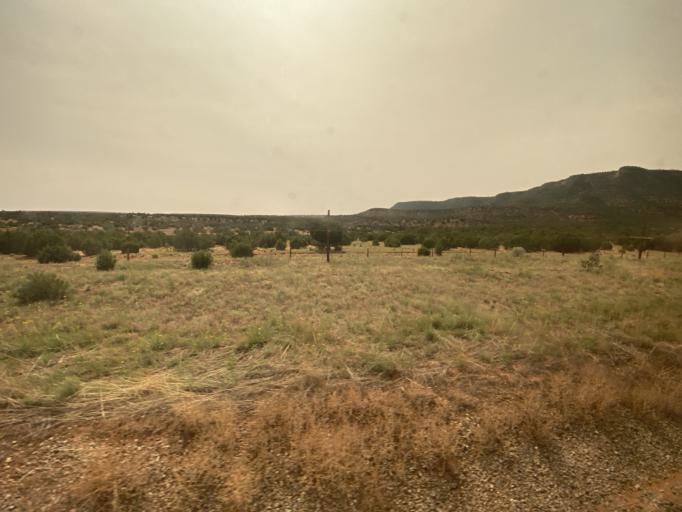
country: US
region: New Mexico
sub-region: San Miguel County
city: Pecos
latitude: 35.3955
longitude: -105.4894
